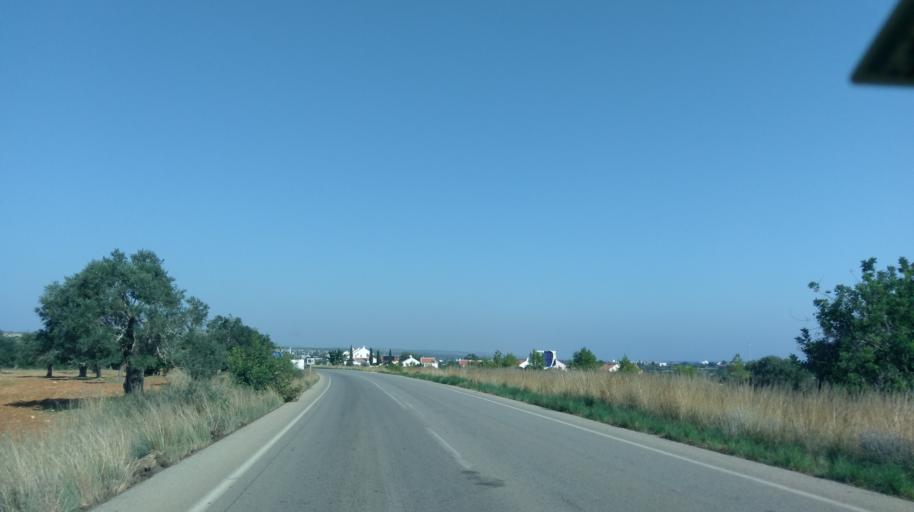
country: CY
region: Ammochostos
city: Leonarisso
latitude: 35.4147
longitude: 34.1183
